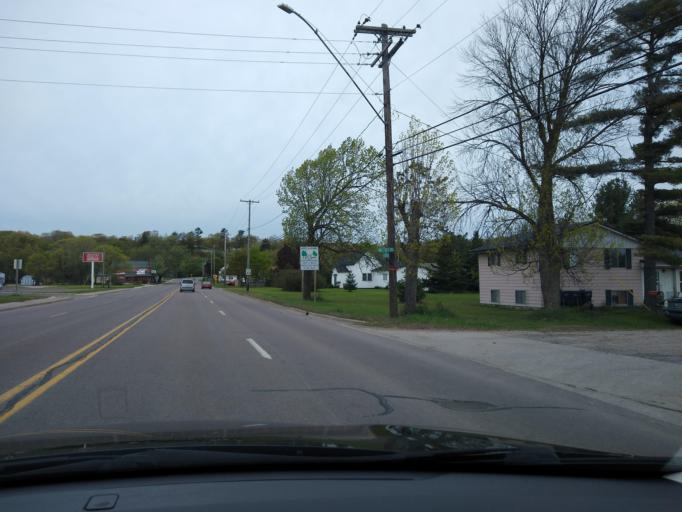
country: US
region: Michigan
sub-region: Delta County
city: Gladstone
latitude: 45.8528
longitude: -87.0270
